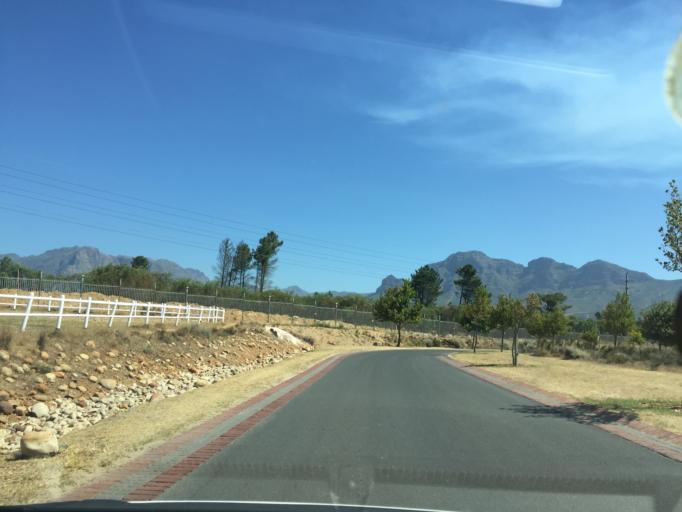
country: ZA
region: Western Cape
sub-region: Cape Winelands District Municipality
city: Paarl
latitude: -33.8068
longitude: 18.9792
